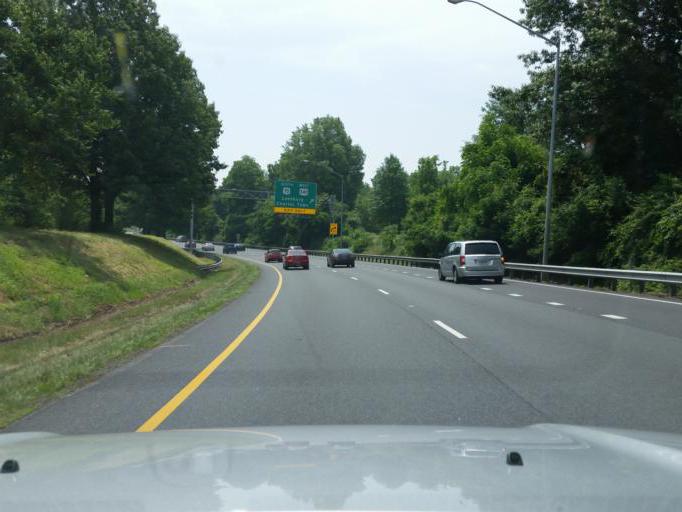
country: US
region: Maryland
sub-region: Frederick County
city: Frederick
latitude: 39.4094
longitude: -77.4365
